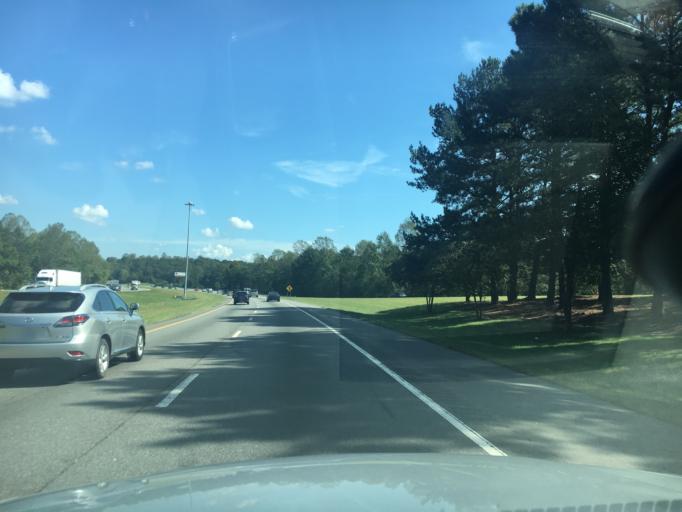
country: US
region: North Carolina
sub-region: Catawba County
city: Conover
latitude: 35.7028
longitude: -81.2607
